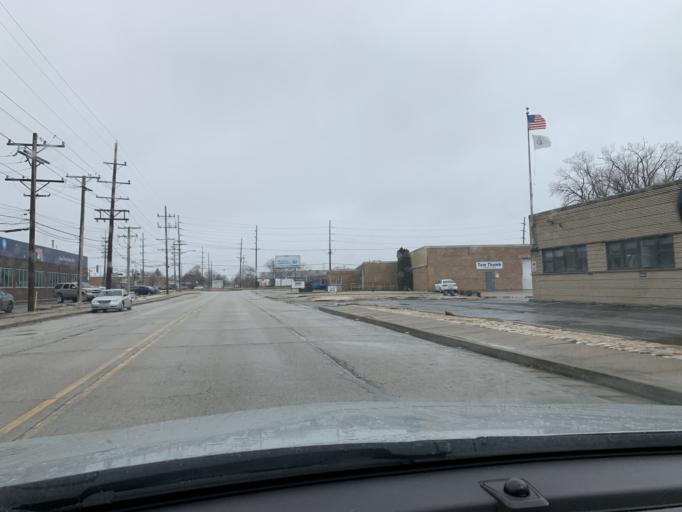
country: US
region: Illinois
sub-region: Cook County
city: Morton Grove
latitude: 42.0181
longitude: -87.7784
